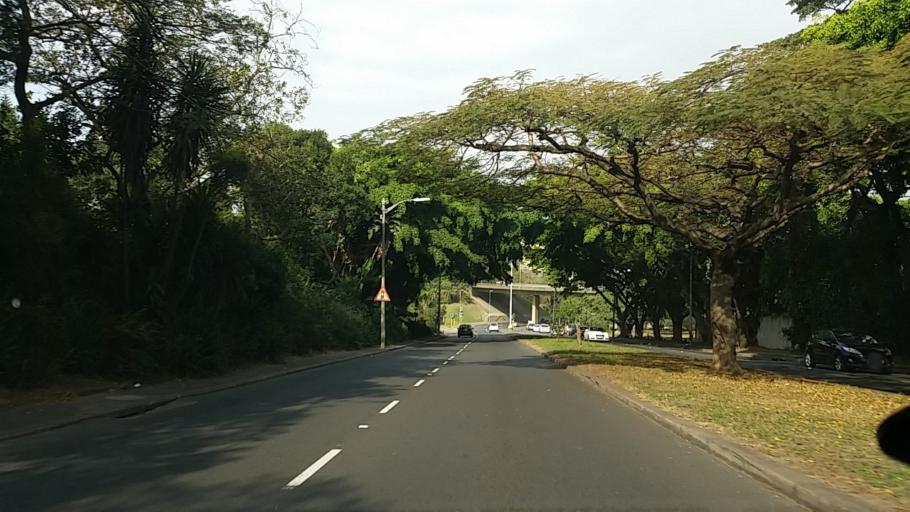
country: ZA
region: KwaZulu-Natal
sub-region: eThekwini Metropolitan Municipality
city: Berea
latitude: -29.8383
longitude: 30.9753
